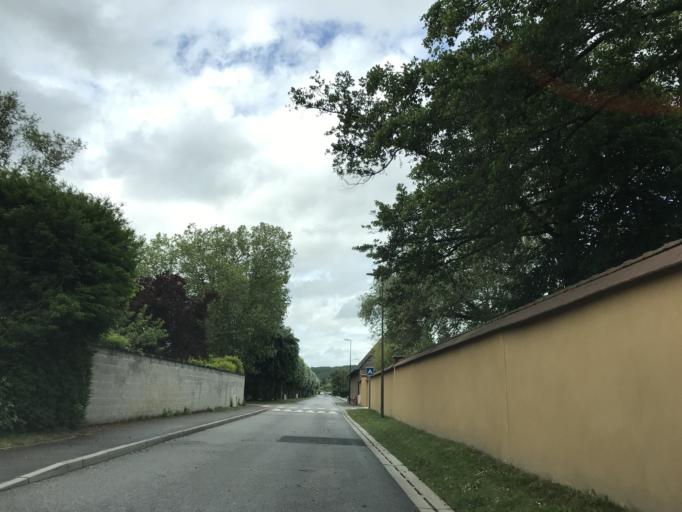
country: FR
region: Haute-Normandie
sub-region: Departement de l'Eure
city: Arnieres-sur-Iton
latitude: 49.0162
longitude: 1.1163
